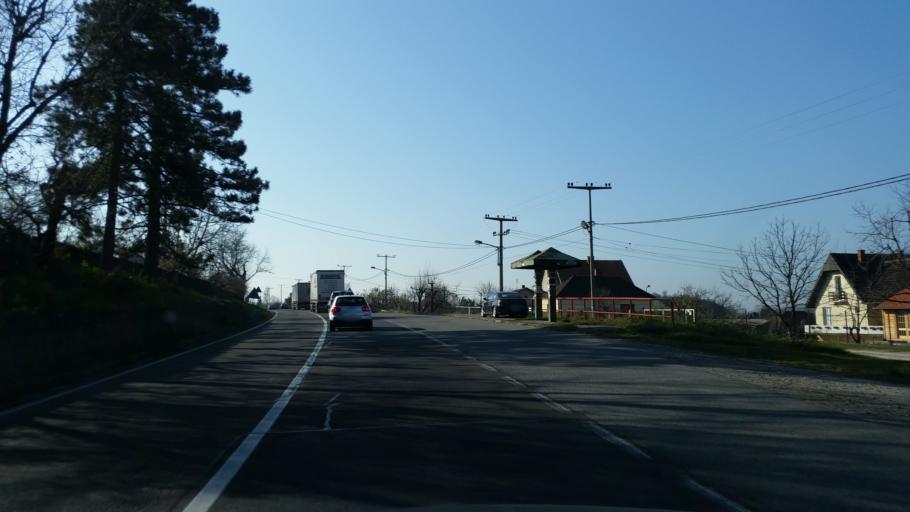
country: RS
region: Central Serbia
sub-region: Kolubarski Okrug
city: Lajkovac
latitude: 44.3632
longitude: 20.1931
